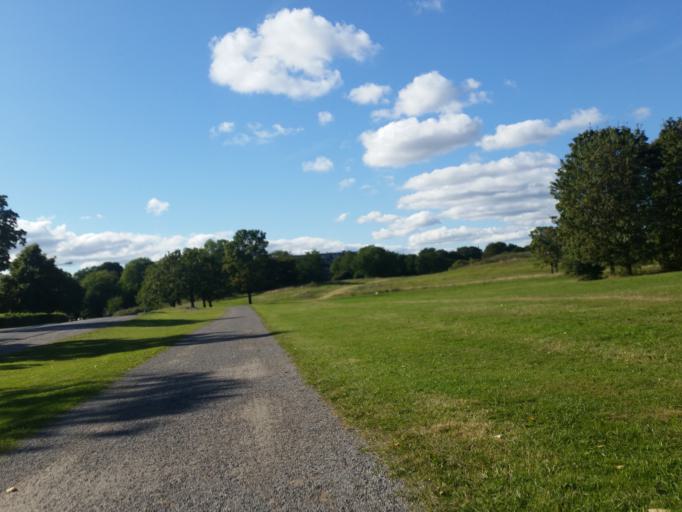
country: SE
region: Stockholm
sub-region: Stockholms Kommun
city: OEstermalm
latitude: 59.3336
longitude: 18.1146
